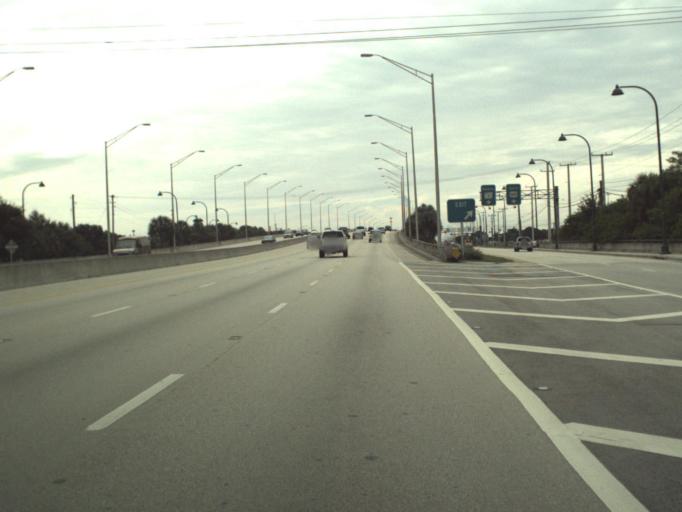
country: US
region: Florida
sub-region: Palm Beach County
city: Royal Palm Beach
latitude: 26.6805
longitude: -80.2073
